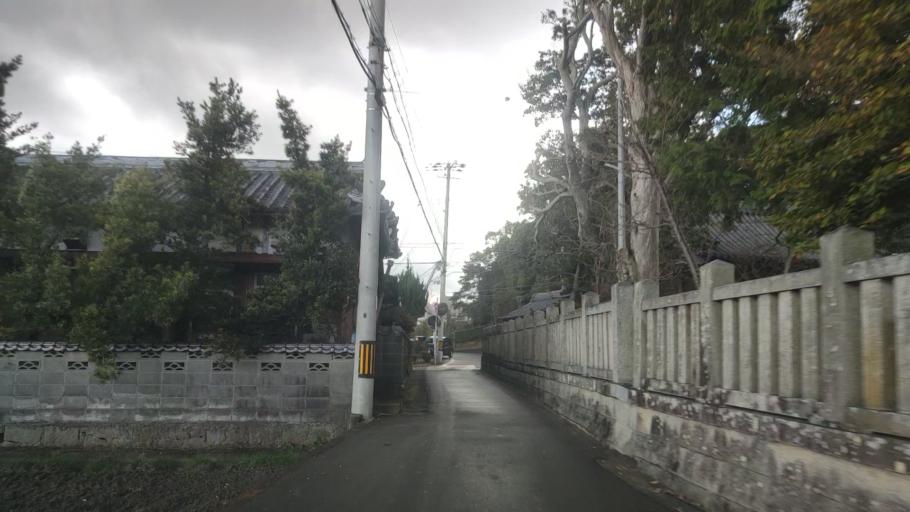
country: JP
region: Hyogo
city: Sumoto
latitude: 34.3317
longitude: 134.8535
